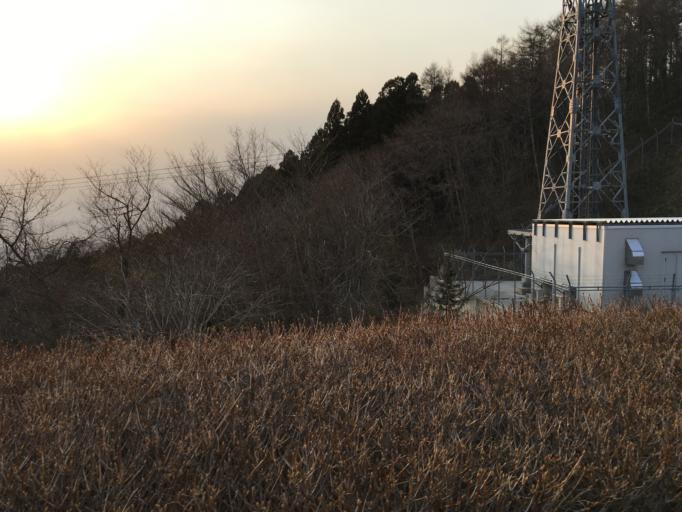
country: JP
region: Iwate
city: Ichinoseki
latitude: 38.9377
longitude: 141.2312
